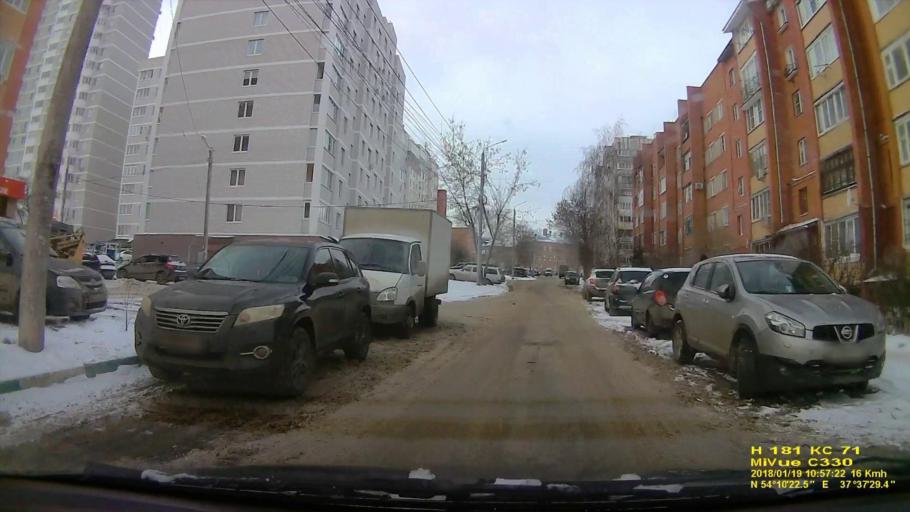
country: RU
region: Tula
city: Tula
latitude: 54.1728
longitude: 37.6247
